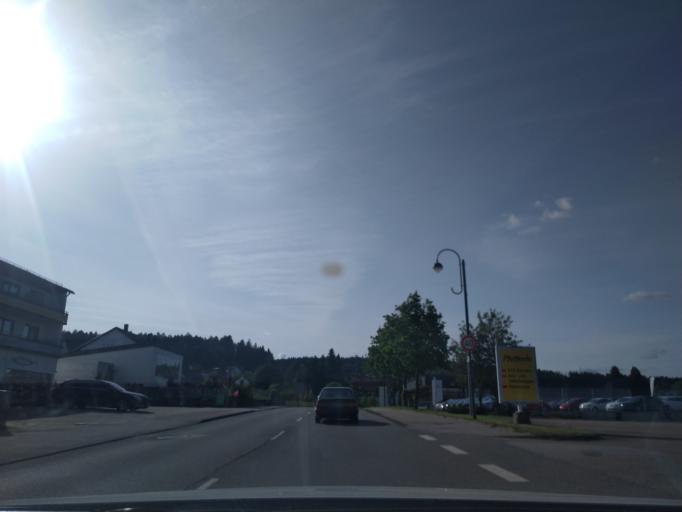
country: DE
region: Baden-Wuerttemberg
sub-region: Karlsruhe Region
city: Lossburg
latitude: 48.4154
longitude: 8.4480
